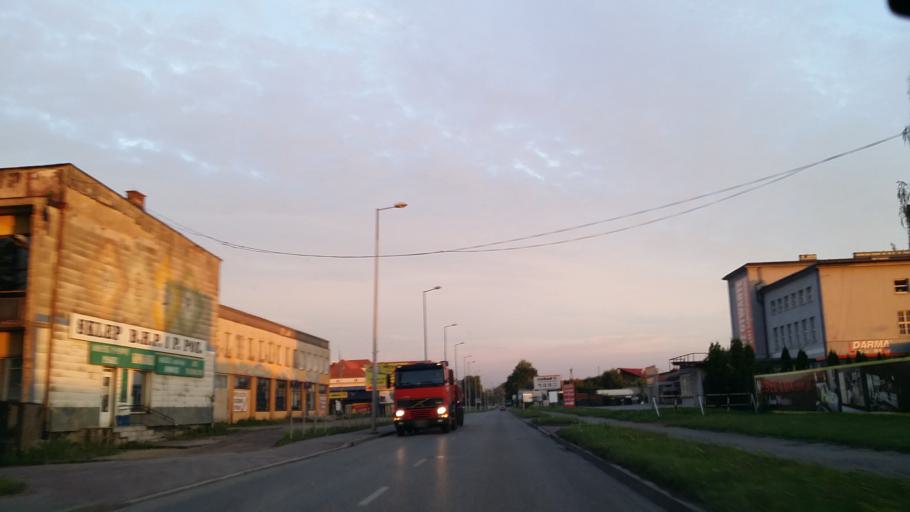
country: PL
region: Lesser Poland Voivodeship
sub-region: Powiat oswiecimski
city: Brzezinka
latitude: 50.0293
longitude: 19.1956
